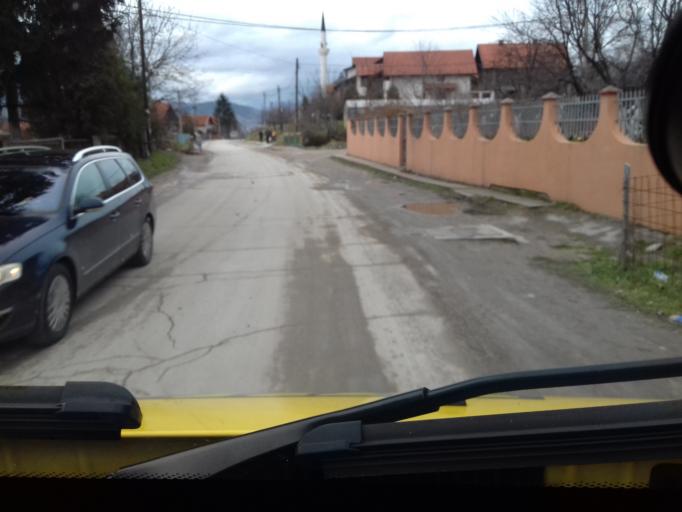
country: BA
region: Federation of Bosnia and Herzegovina
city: Zenica
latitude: 44.1865
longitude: 17.9655
